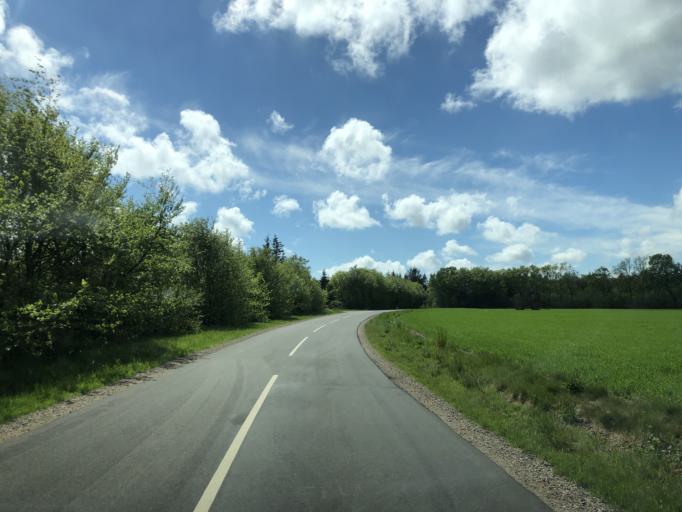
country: DK
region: Central Jutland
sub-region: Ringkobing-Skjern Kommune
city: Tarm
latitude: 55.9414
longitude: 8.5682
